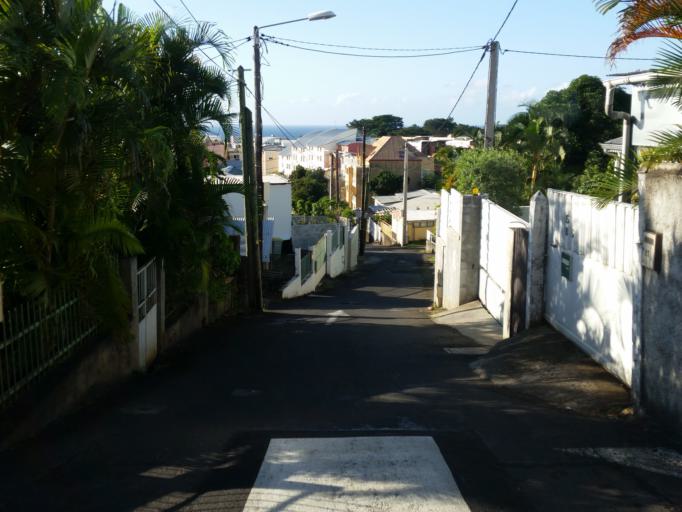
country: RE
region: Reunion
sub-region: Reunion
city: Saint-Denis
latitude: -20.8983
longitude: 55.4694
